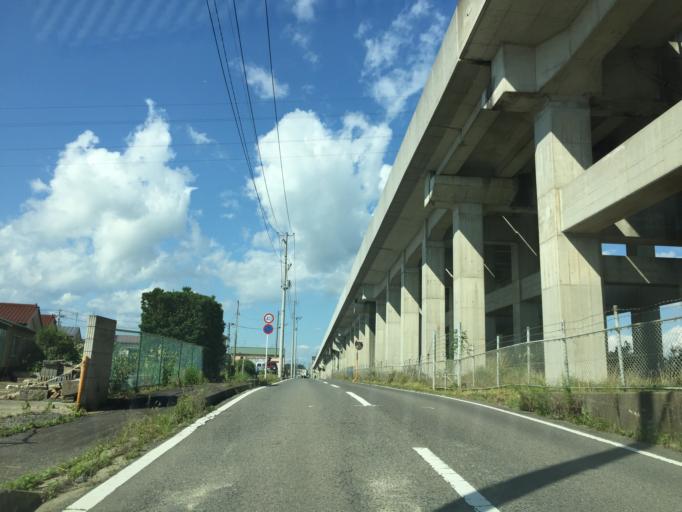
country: JP
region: Fukushima
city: Koriyama
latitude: 37.4132
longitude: 140.3928
